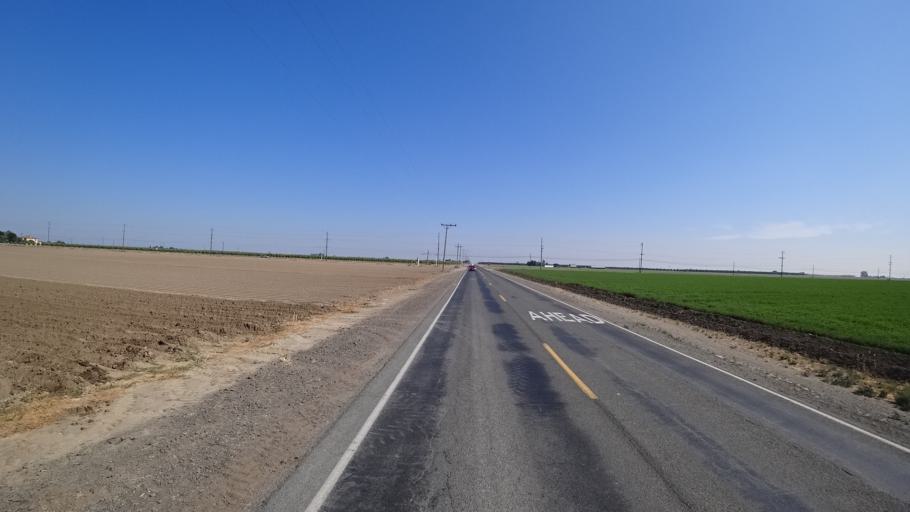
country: US
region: California
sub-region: Kings County
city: Home Garden
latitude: 36.3411
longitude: -119.5651
